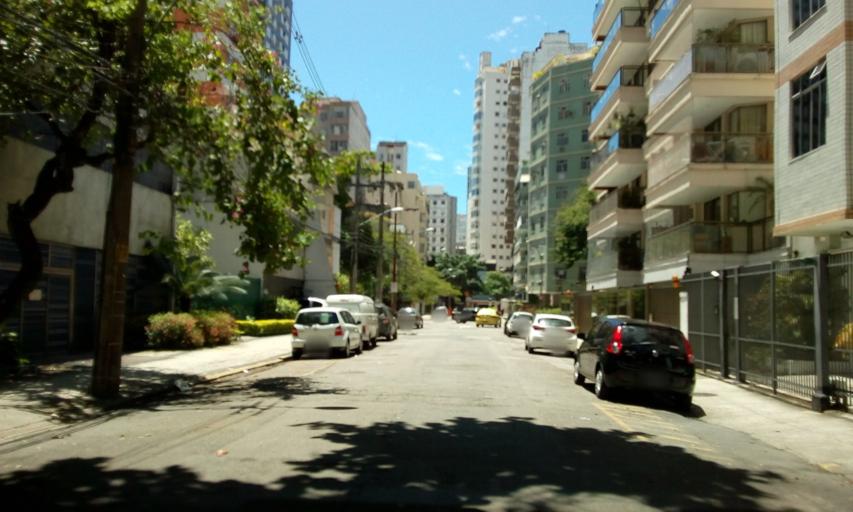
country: BR
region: Rio de Janeiro
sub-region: Rio De Janeiro
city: Rio de Janeiro
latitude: -22.9398
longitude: -43.1803
